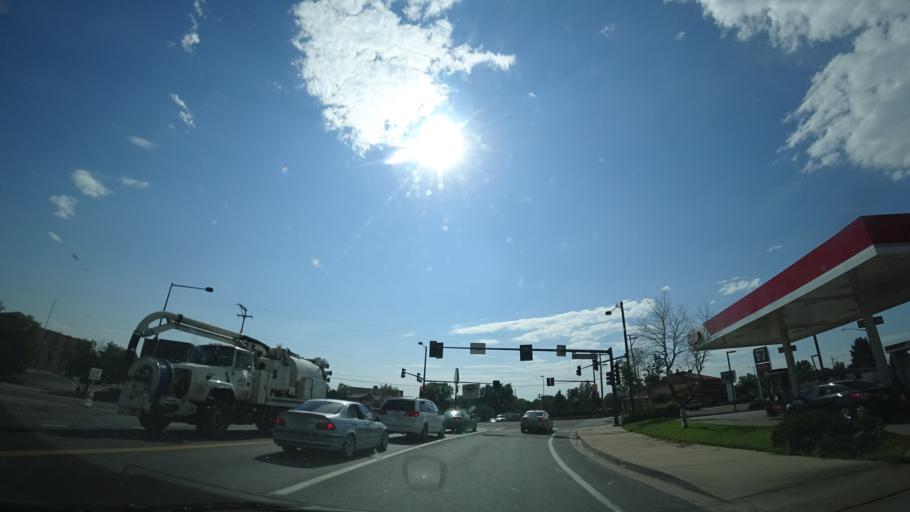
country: US
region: Colorado
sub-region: Jefferson County
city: Lakewood
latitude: 39.7186
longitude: -105.0538
